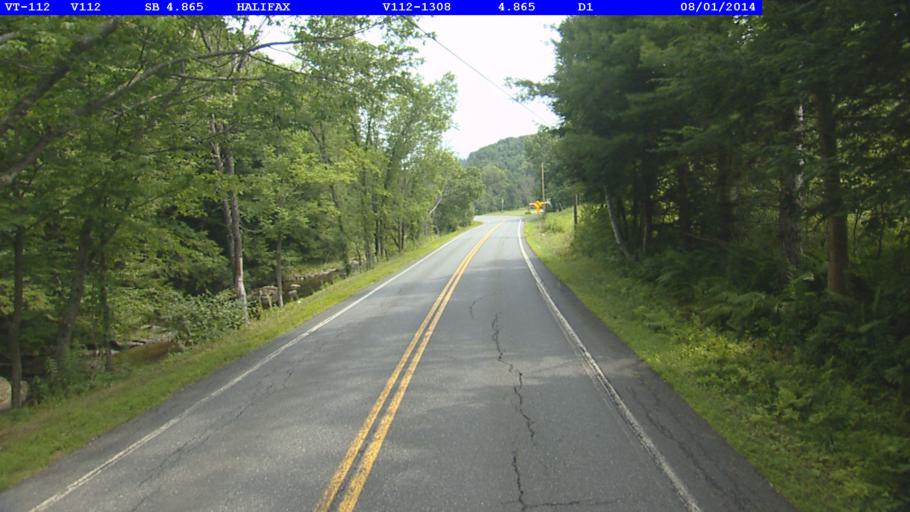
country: US
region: Massachusetts
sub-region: Franklin County
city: Colrain
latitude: 42.7670
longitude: -72.7958
